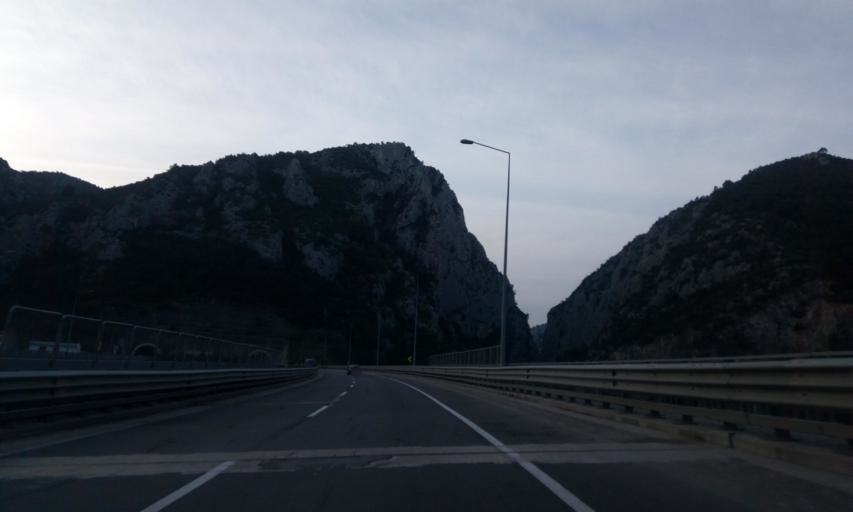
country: TR
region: Bilecik
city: Vezirhan
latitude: 40.1939
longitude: 30.0133
